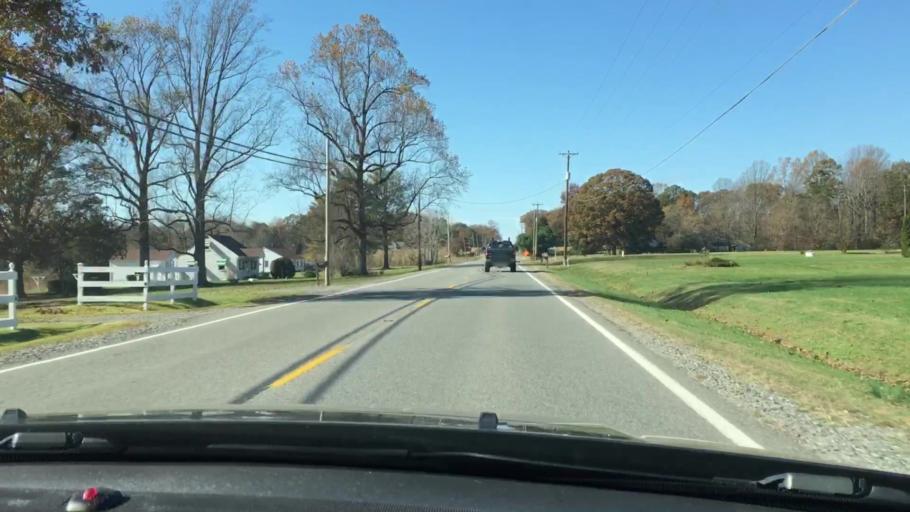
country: US
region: Virginia
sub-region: King William County
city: Central Garage
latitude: 37.7319
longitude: -77.1099
